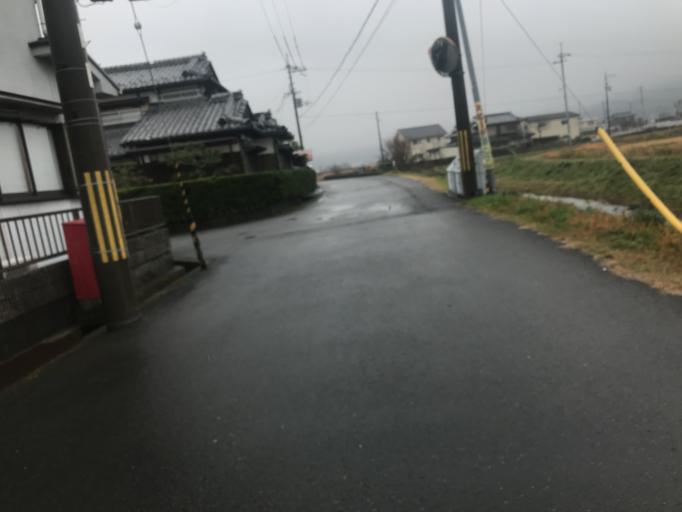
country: JP
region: Kyoto
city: Kameoka
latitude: 34.9956
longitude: 135.5430
